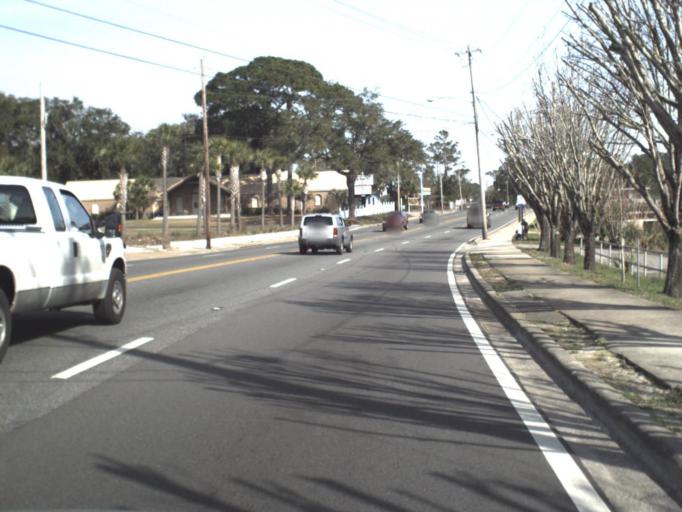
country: US
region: Florida
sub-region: Bay County
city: Panama City
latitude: 30.1572
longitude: -85.6410
